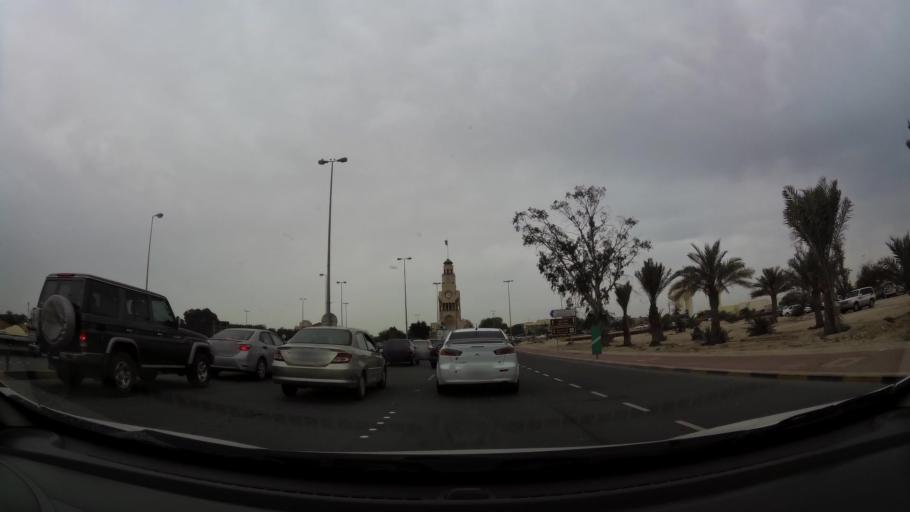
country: BH
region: Northern
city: Ar Rifa'
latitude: 26.1351
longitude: 50.5380
